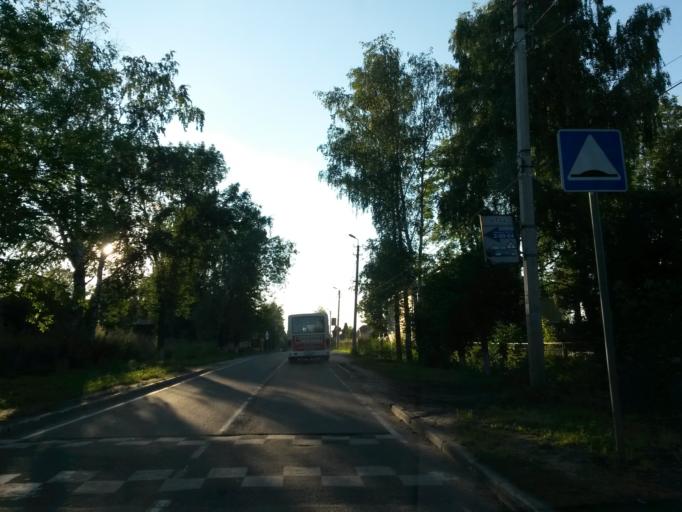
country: RU
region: Jaroslavl
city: Tutayev
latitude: 57.8709
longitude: 39.5306
